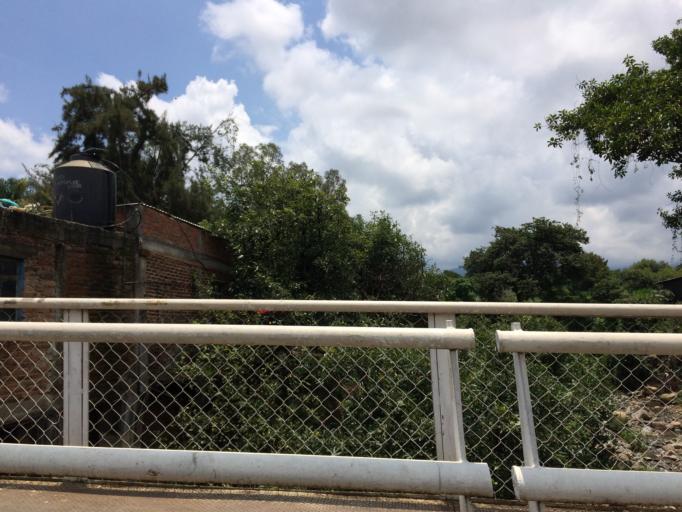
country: MX
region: Michoacan
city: Periban de Ramos
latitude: 19.5251
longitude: -102.4134
